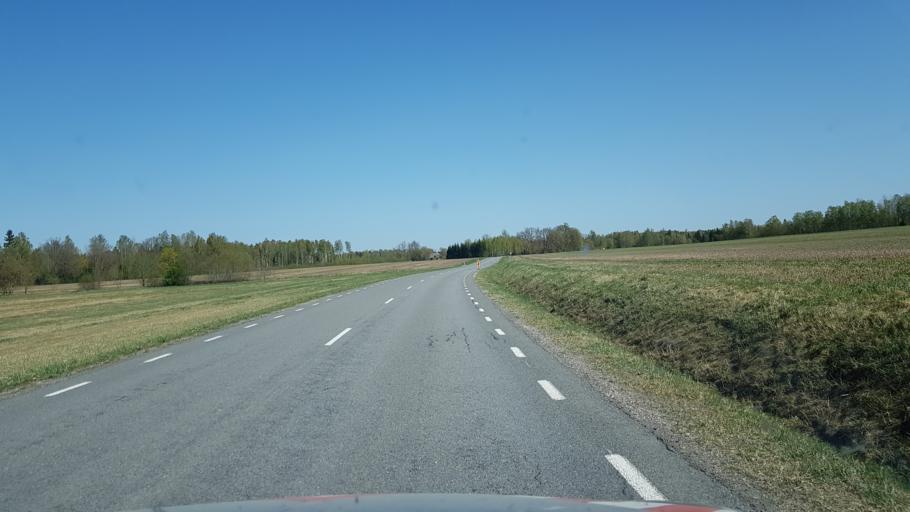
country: EE
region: Viljandimaa
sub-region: Suure-Jaani vald
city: Suure-Jaani
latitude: 58.4921
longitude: 25.4491
